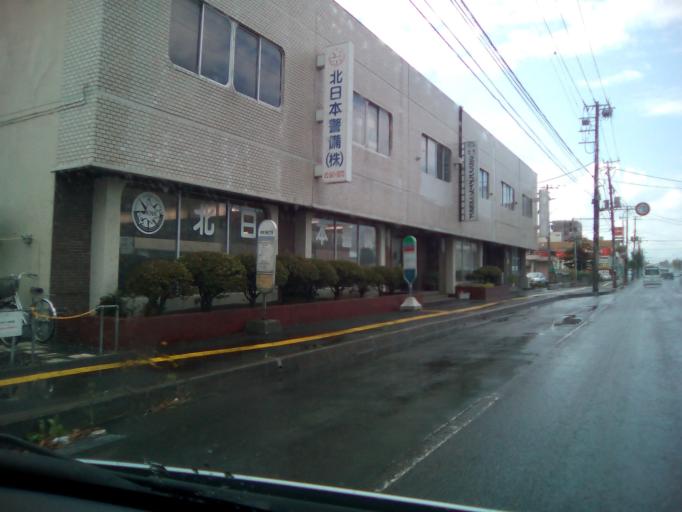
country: JP
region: Hokkaido
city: Sapporo
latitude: 43.0567
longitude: 141.3954
